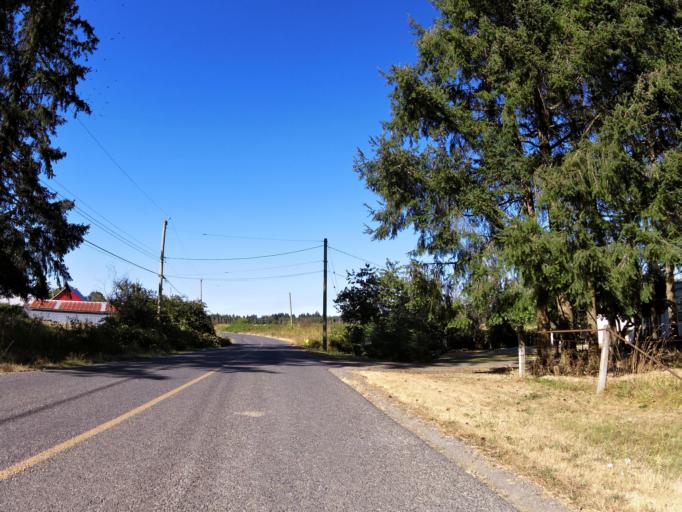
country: CA
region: British Columbia
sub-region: Cowichan Valley Regional District
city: Ladysmith
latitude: 49.0823
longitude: -123.8436
